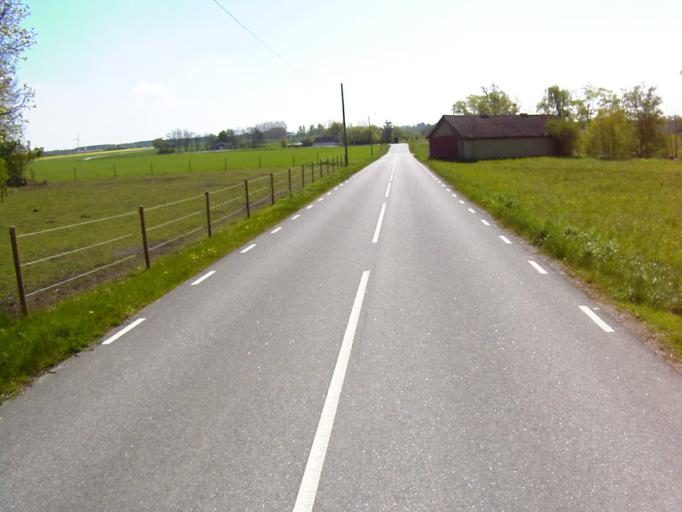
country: SE
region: Skane
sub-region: Kristianstads Kommun
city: Fjalkinge
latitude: 56.0090
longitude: 14.2470
